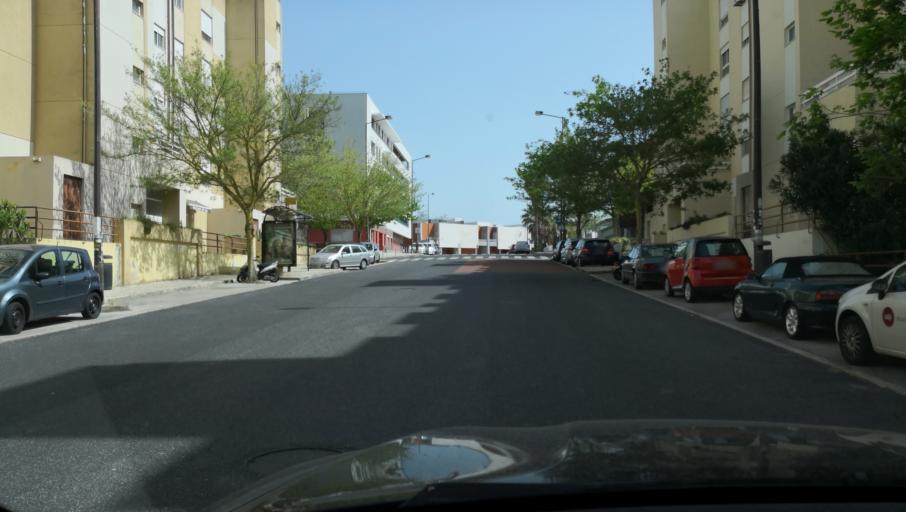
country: PT
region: Lisbon
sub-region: Odivelas
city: Olival do Basto
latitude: 38.7684
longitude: -9.1683
